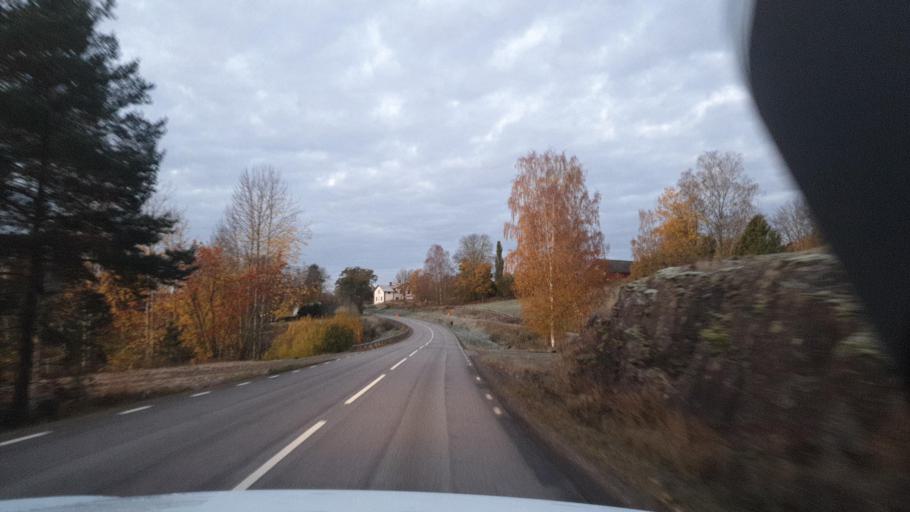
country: SE
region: Vaermland
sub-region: Eda Kommun
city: Charlottenberg
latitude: 59.8112
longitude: 12.2557
